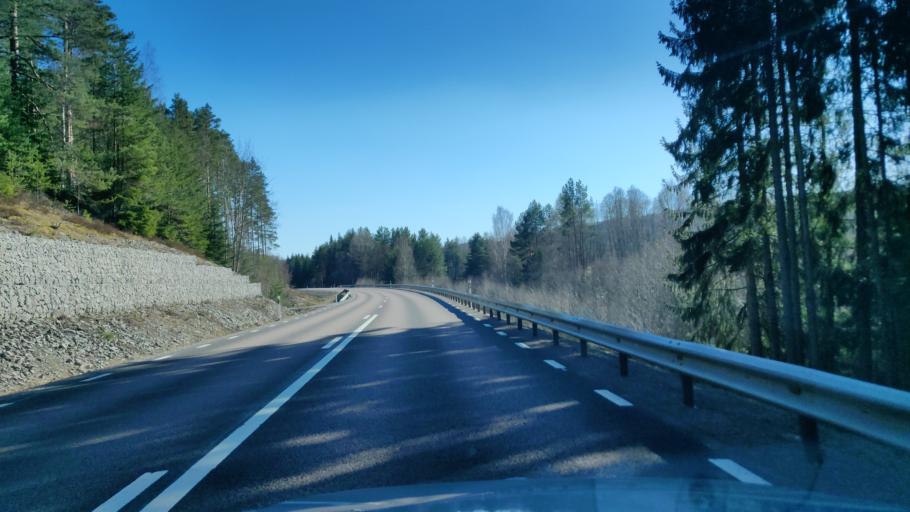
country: SE
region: Vaermland
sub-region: Hagfors Kommun
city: Hagfors
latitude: 59.9301
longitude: 13.6748
